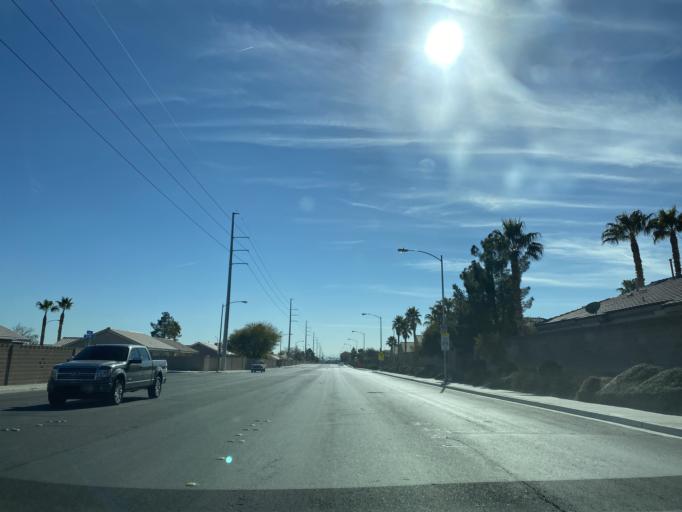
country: US
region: Nevada
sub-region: Clark County
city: North Las Vegas
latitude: 36.2594
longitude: -115.1440
